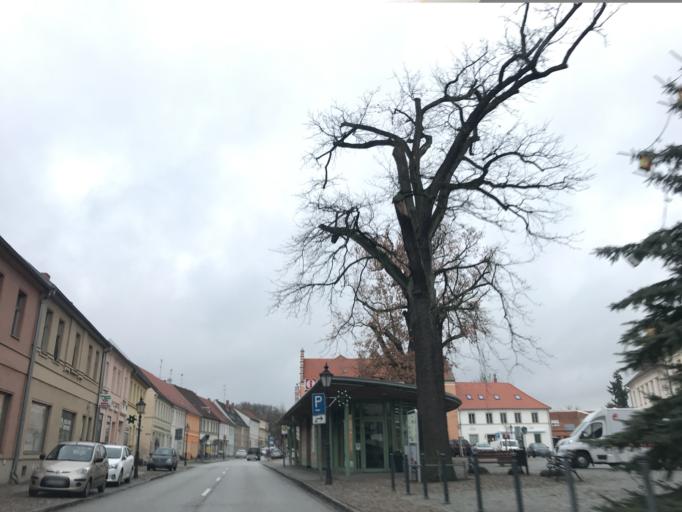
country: DE
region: Brandenburg
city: Lindow
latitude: 52.9713
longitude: 12.9880
